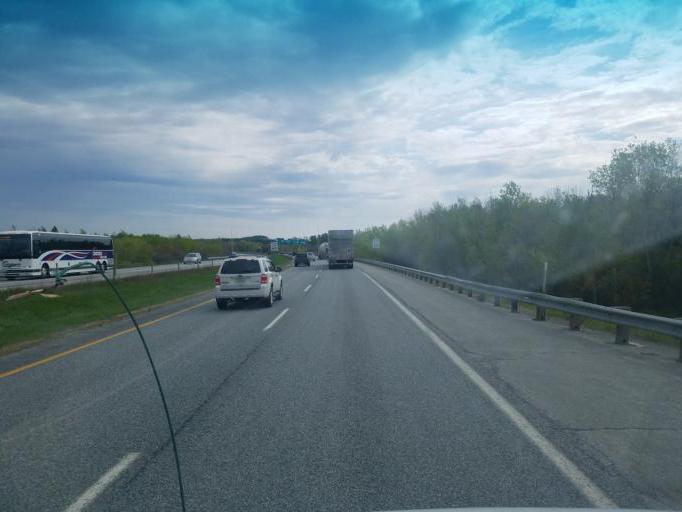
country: US
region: Maine
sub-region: Penobscot County
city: Bangor
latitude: 44.7817
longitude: -68.8140
